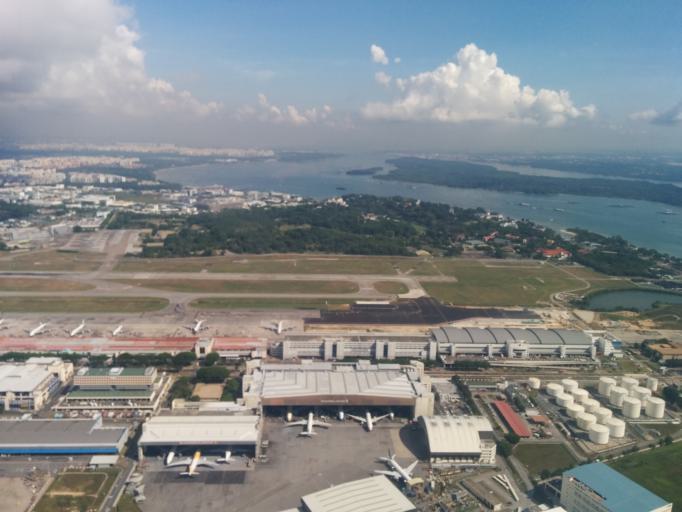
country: MY
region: Johor
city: Kampung Pasir Gudang Baru
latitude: 1.3736
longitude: 104.0040
